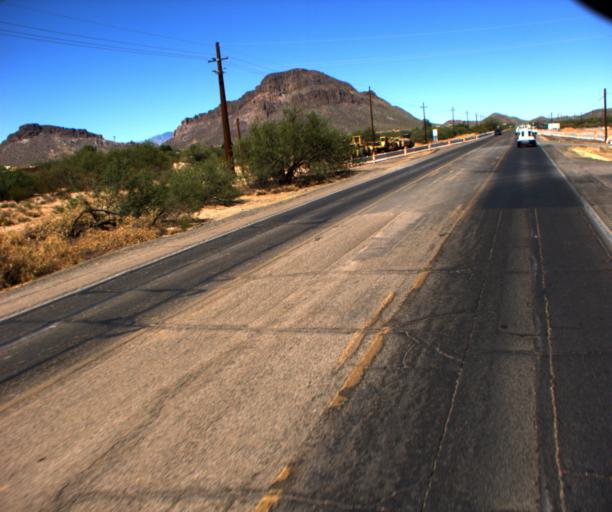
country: US
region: Arizona
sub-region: Pima County
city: Tucson Estates
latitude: 32.1670
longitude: -111.0868
